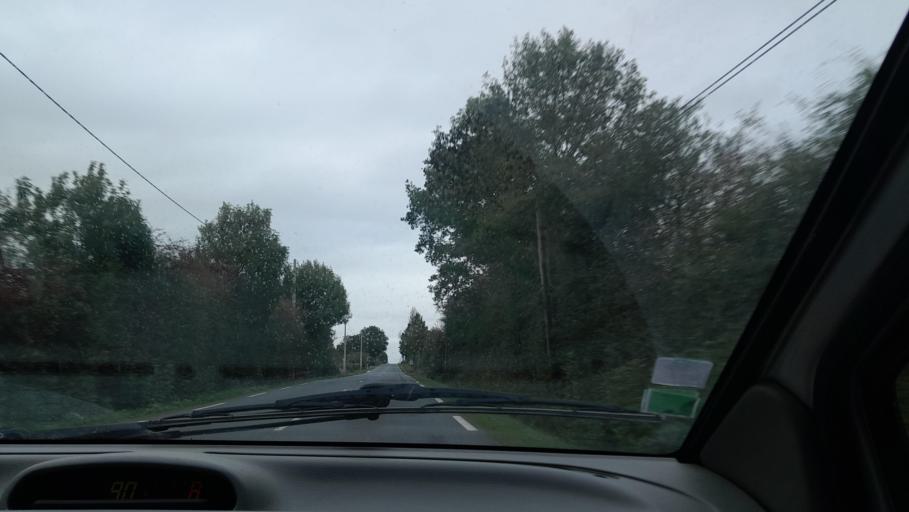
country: FR
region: Pays de la Loire
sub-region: Departement de Maine-et-Loire
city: Pouance
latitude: 47.6683
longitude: -1.1902
